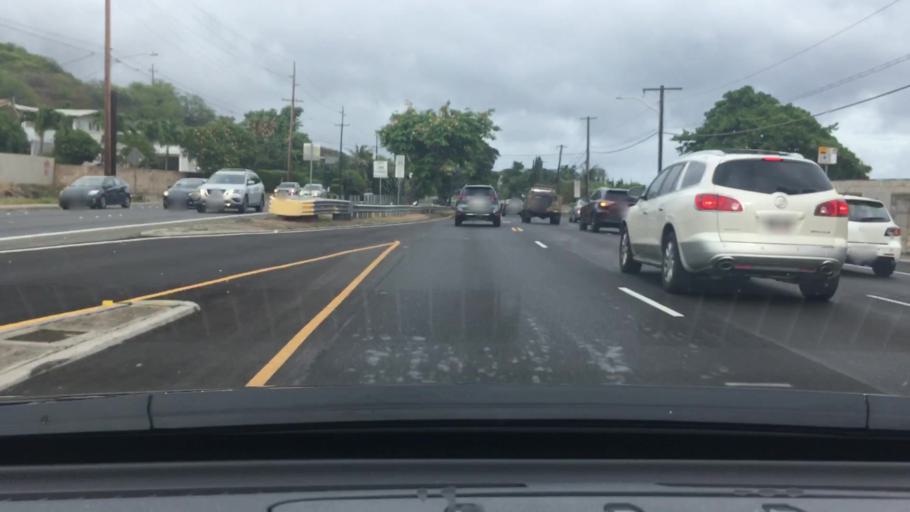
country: US
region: Hawaii
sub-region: Honolulu County
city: Honolulu
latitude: 21.2778
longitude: -157.7795
